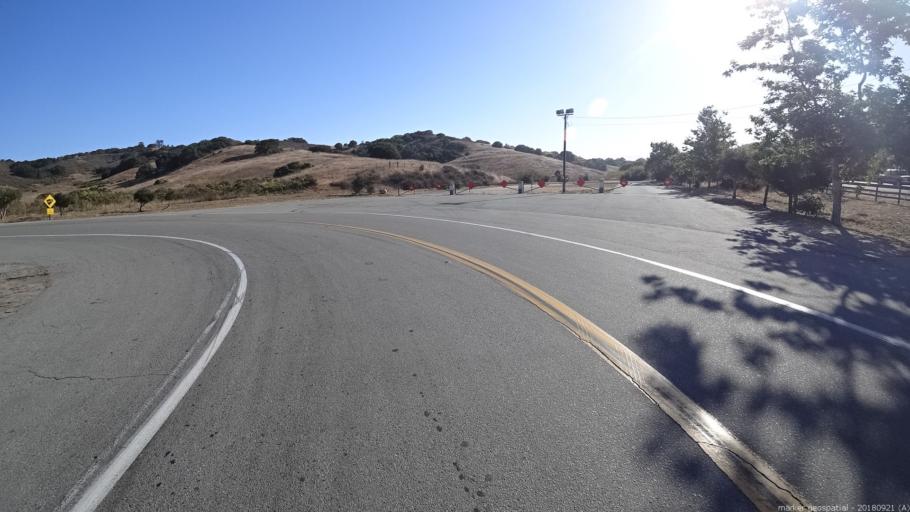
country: US
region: California
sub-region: Monterey County
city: Carmel Valley Village
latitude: 36.5707
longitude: -121.7610
